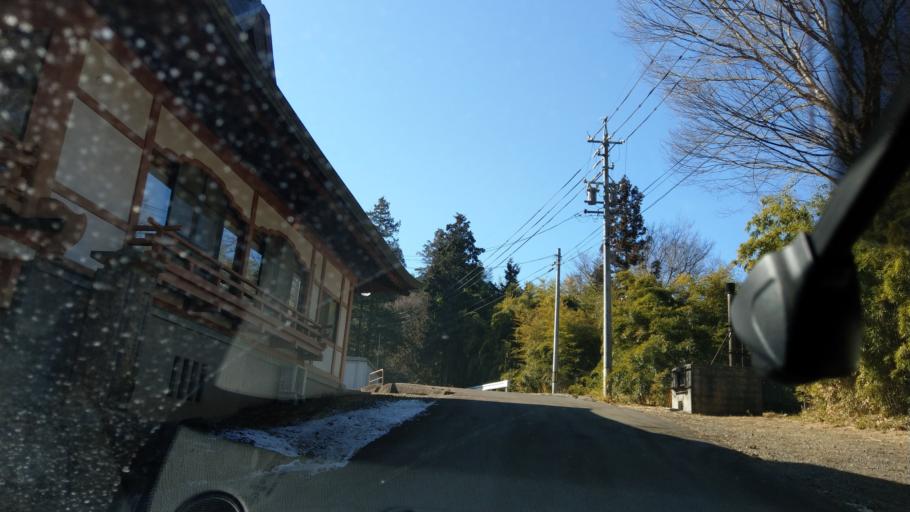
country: JP
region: Nagano
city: Saku
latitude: 36.2169
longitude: 138.4492
